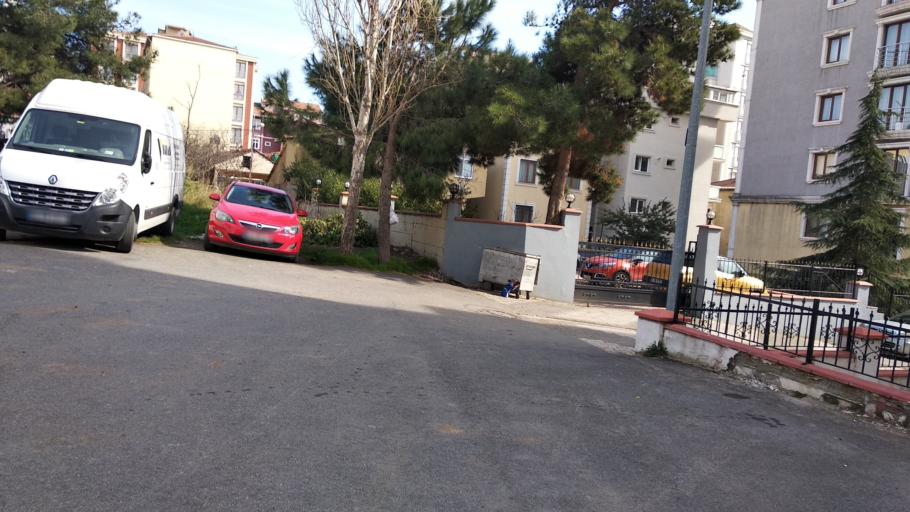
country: TR
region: Istanbul
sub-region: Atasehir
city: Atasehir
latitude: 40.9853
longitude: 29.1134
